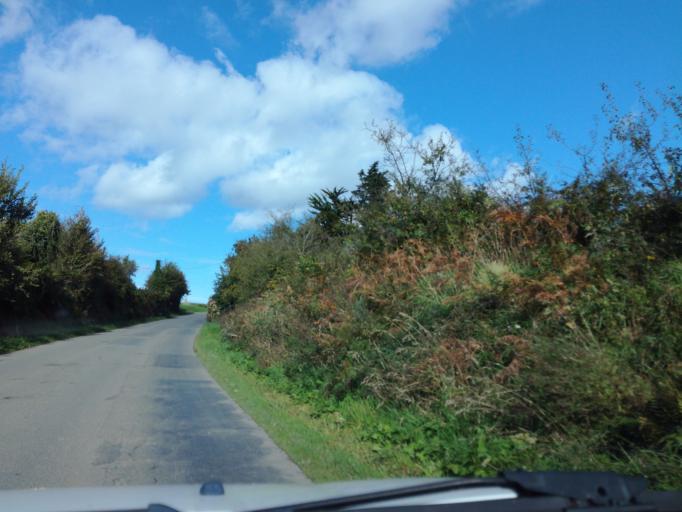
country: FR
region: Brittany
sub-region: Departement des Cotes-d'Armor
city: Langoat
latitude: 48.7787
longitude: -3.2836
